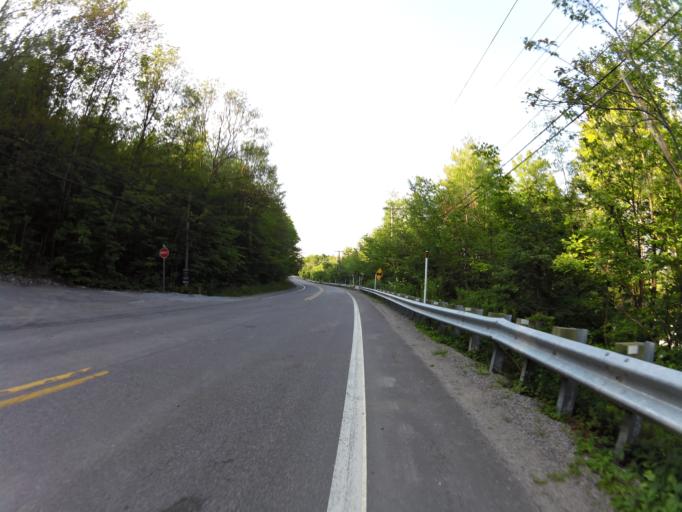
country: CA
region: Quebec
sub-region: Outaouais
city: Wakefield
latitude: 45.5472
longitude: -75.8211
